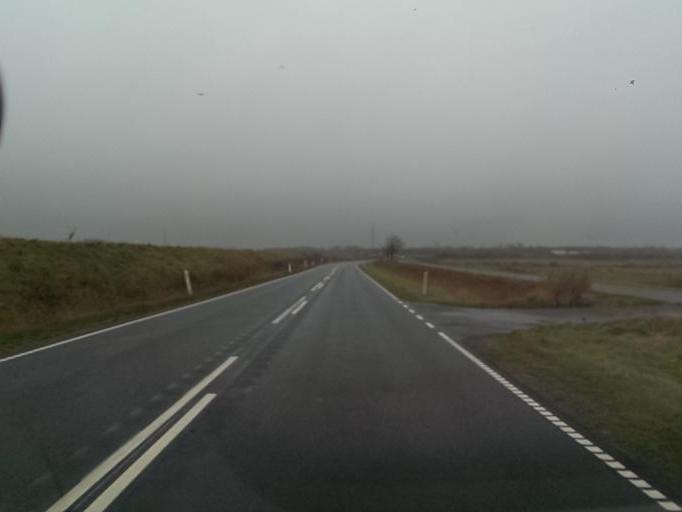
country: DK
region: South Denmark
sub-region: Esbjerg Kommune
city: Tjaereborg
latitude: 55.4648
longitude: 8.5437
